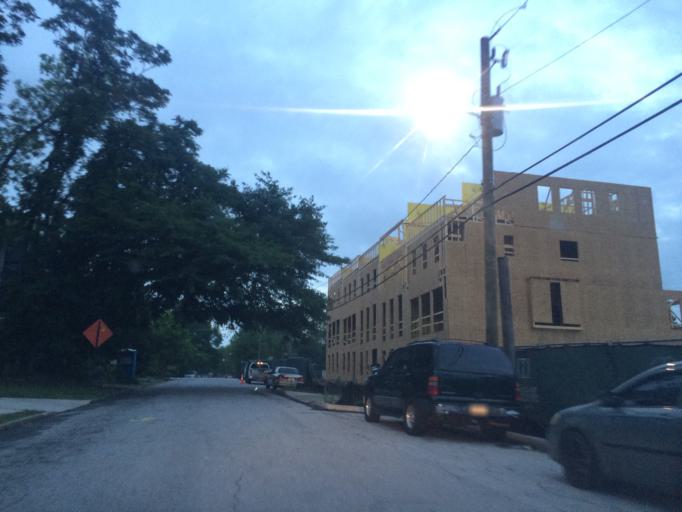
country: US
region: Georgia
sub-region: Fulton County
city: Atlanta
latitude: 33.7640
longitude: -84.3666
